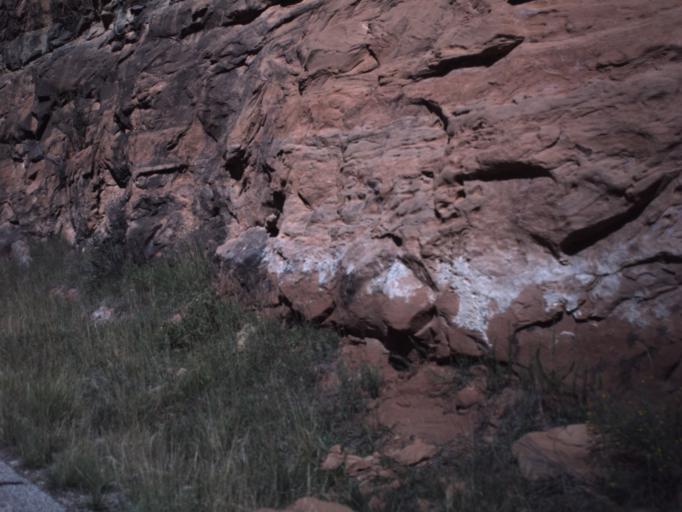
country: US
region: Utah
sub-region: San Juan County
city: Monticello
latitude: 38.3288
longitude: -109.0762
